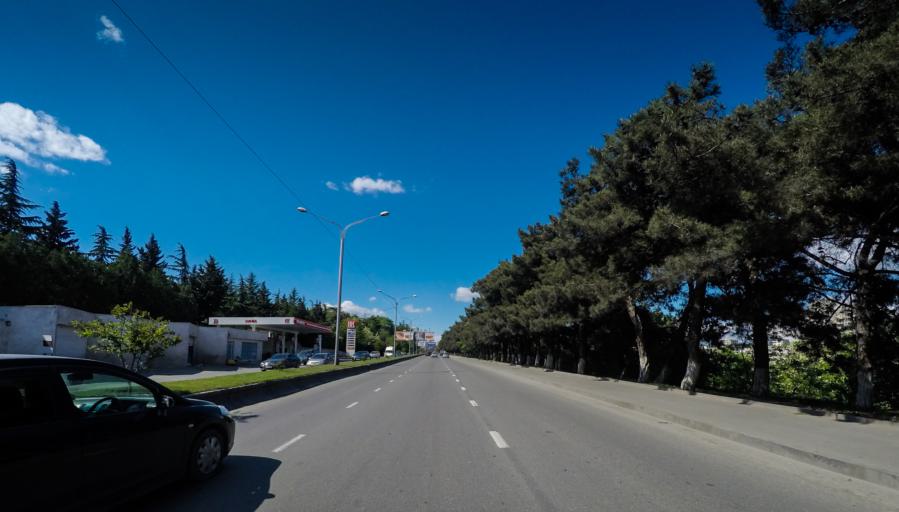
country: GE
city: Zahesi
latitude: 41.7499
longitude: 44.7704
